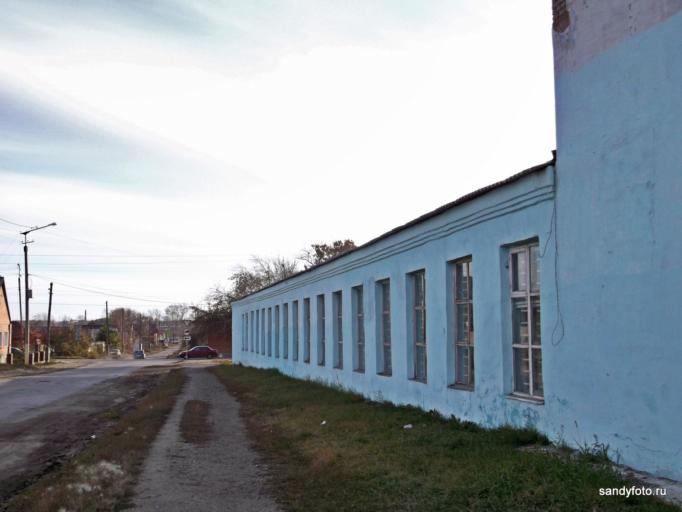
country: RU
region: Chelyabinsk
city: Troitsk
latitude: 54.0965
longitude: 61.5880
